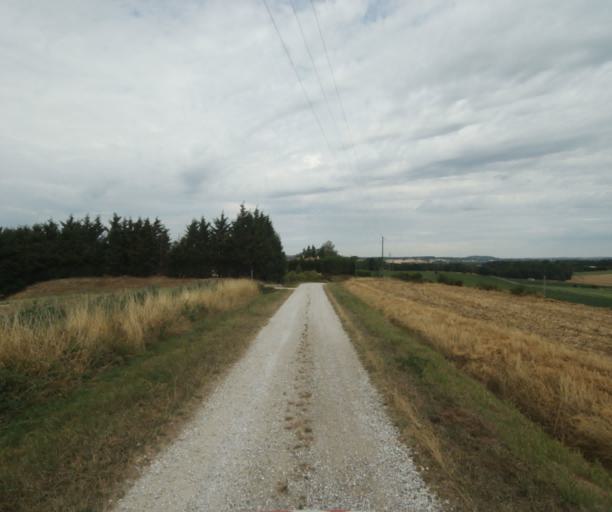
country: FR
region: Midi-Pyrenees
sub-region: Departement de la Haute-Garonne
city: Revel
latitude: 43.4346
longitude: 1.9617
